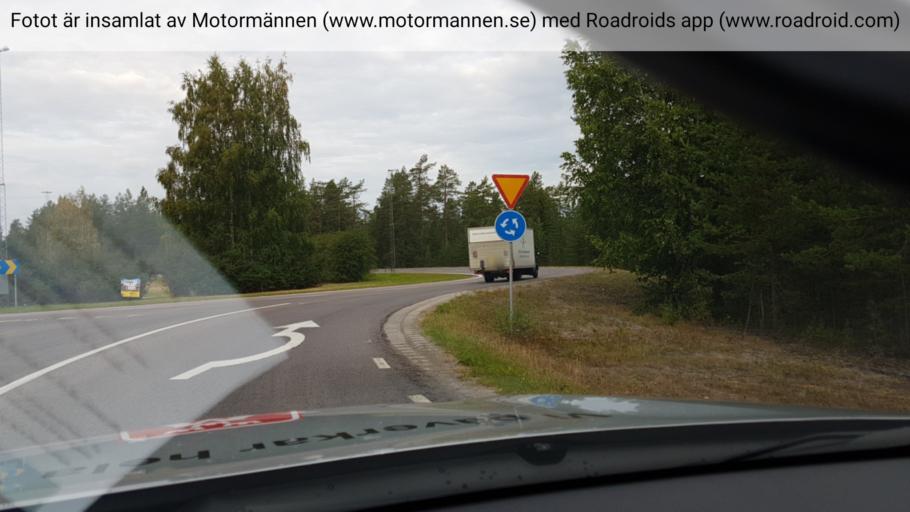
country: SE
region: Norrbotten
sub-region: Lulea Kommun
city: Bergnaset
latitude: 65.5791
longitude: 22.0764
